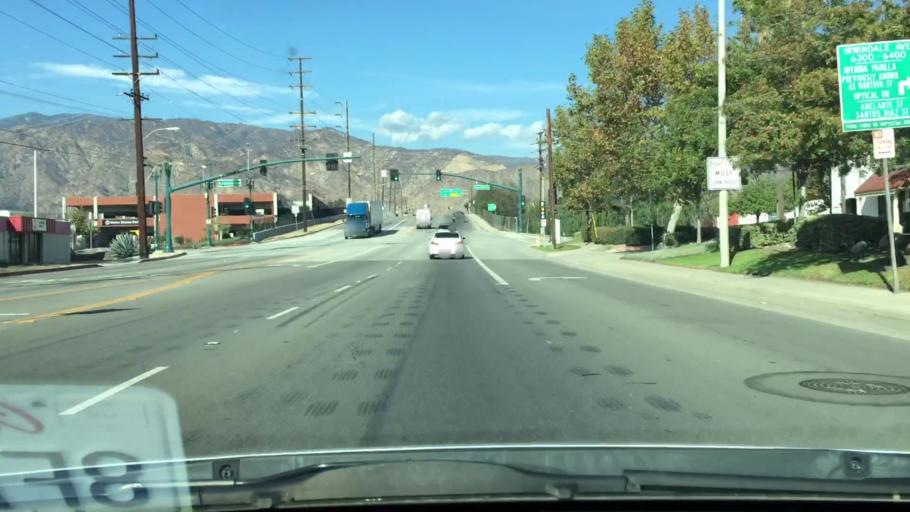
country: US
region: California
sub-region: Los Angeles County
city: Irwindale
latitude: 34.1259
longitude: -117.9337
